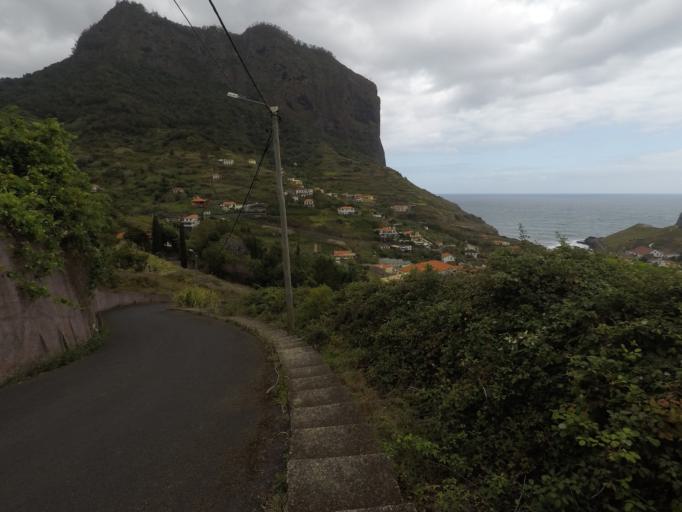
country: PT
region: Madeira
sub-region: Santana
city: Santana
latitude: 32.7697
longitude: -16.8311
